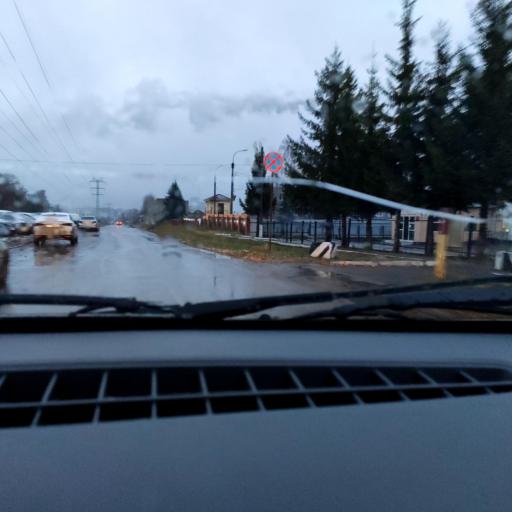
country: RU
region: Bashkortostan
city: Avdon
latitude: 54.6845
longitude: 55.8041
